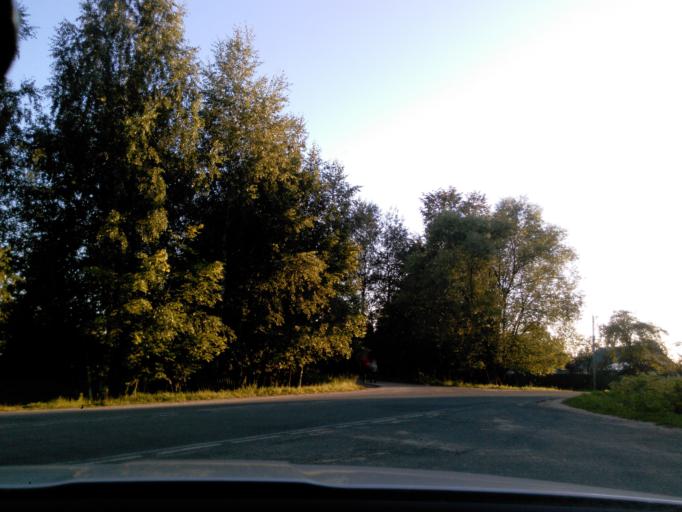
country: RU
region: Moskovskaya
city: Solnechnogorsk
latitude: 56.1281
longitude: 36.8574
